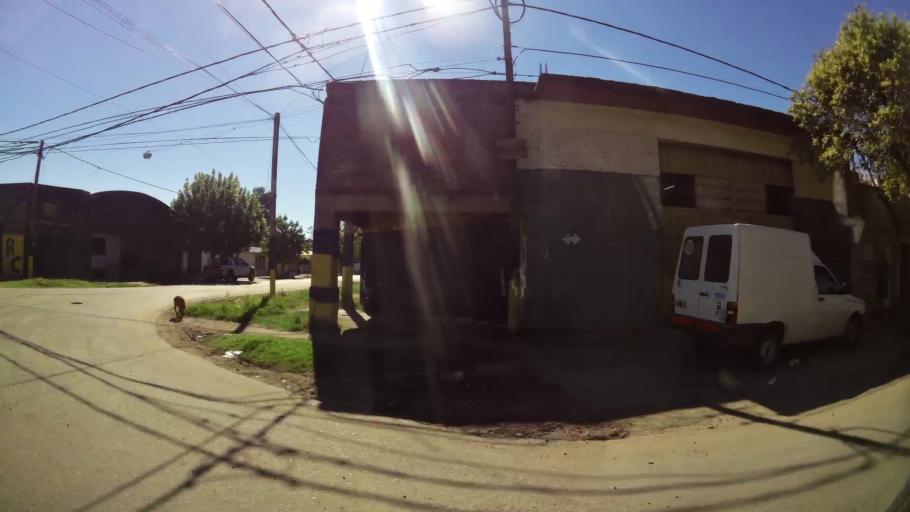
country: AR
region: Santa Fe
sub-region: Departamento de Rosario
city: Rosario
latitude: -32.9533
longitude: -60.6912
